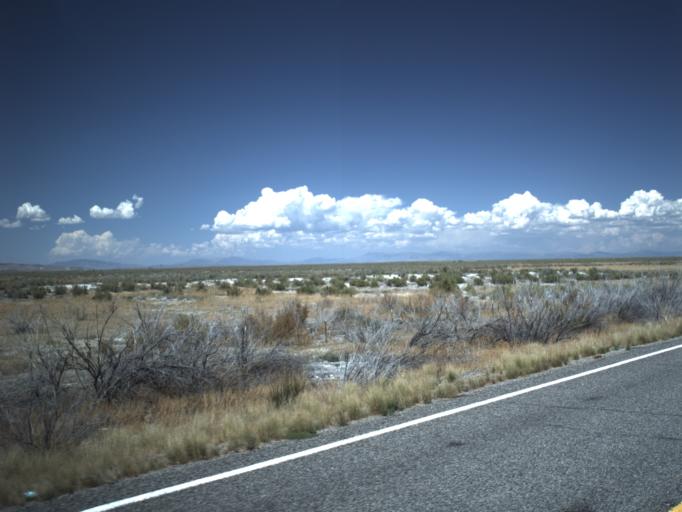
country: US
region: Utah
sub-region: Millard County
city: Delta
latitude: 39.2834
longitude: -112.8405
